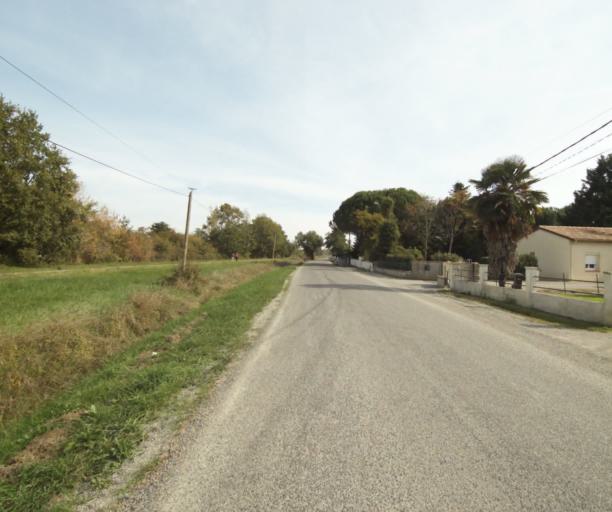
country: FR
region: Midi-Pyrenees
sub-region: Departement du Tarn-et-Garonne
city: Labastide-Saint-Pierre
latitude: 43.9139
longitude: 1.3747
